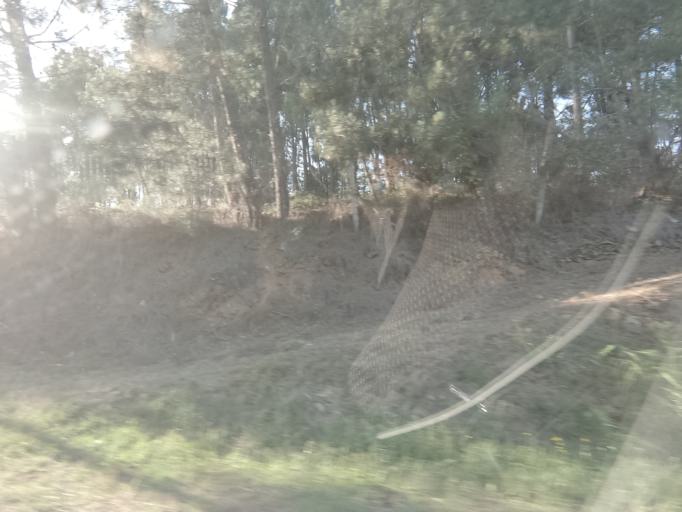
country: PT
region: Vila Real
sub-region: Sabrosa
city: Vilela
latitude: 41.2706
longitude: -7.6527
